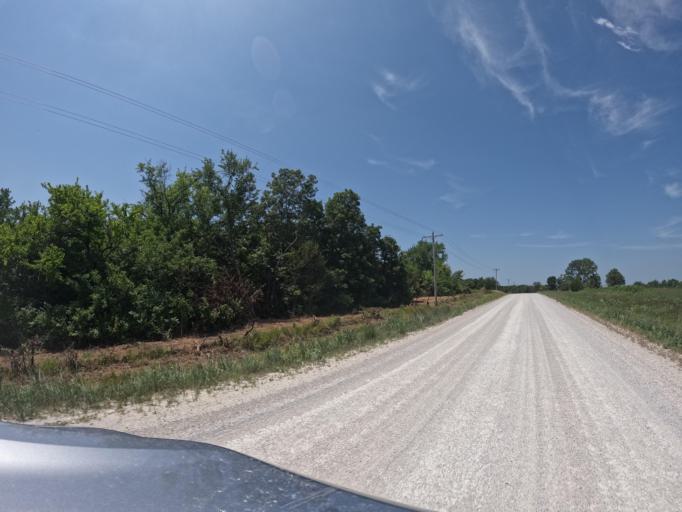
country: US
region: Iowa
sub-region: Henry County
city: Mount Pleasant
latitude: 40.9048
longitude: -91.5421
